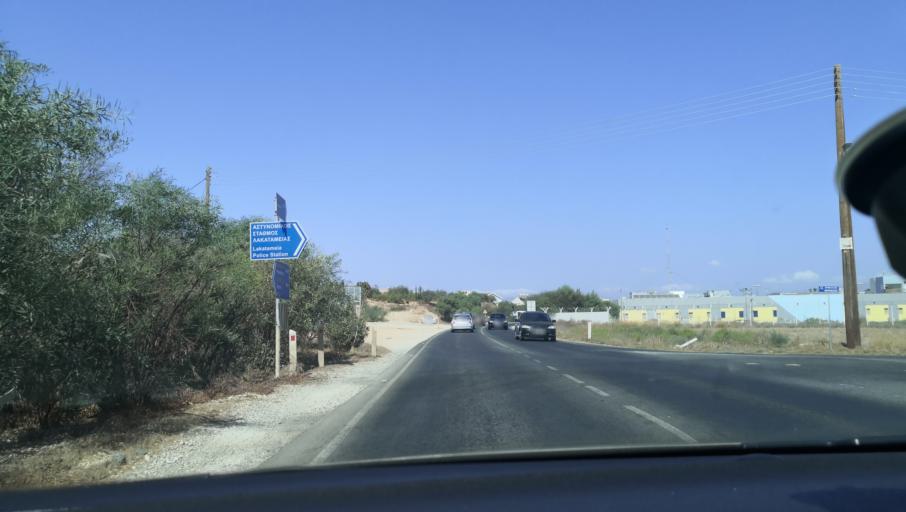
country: CY
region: Lefkosia
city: Kato Deftera
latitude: 35.1094
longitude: 33.2847
